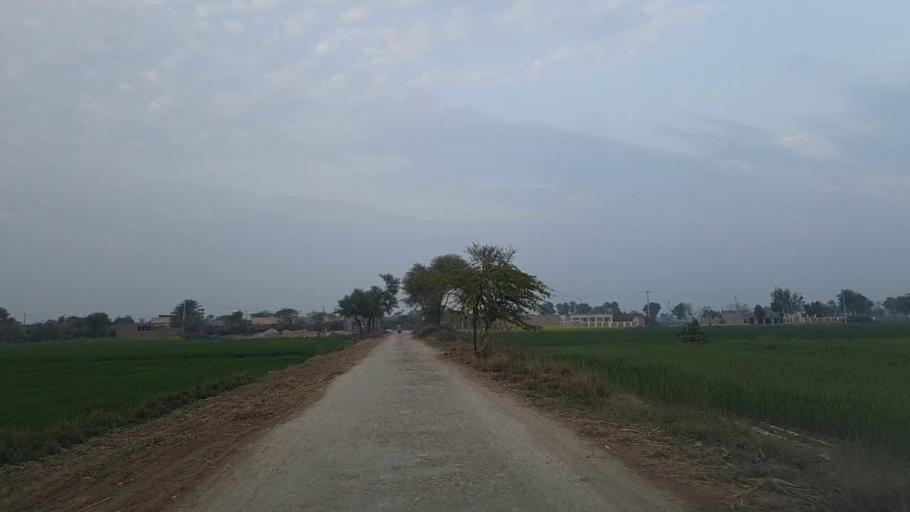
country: PK
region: Sindh
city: Jam Sahib
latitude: 26.2971
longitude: 68.5934
